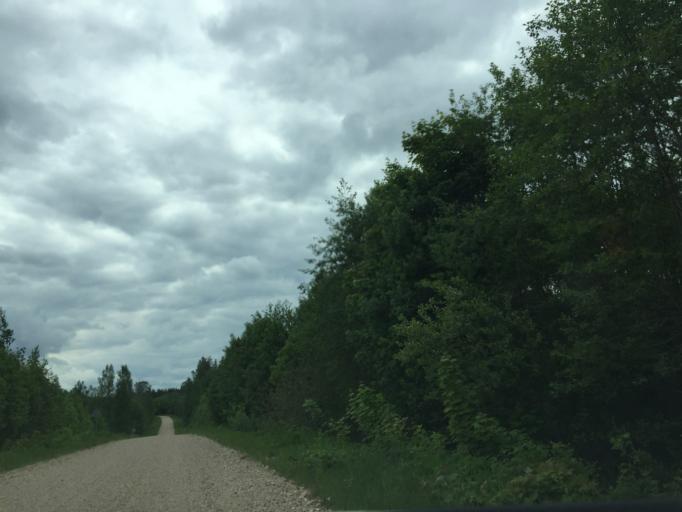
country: LV
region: Dagda
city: Dagda
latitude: 56.1921
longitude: 27.2909
